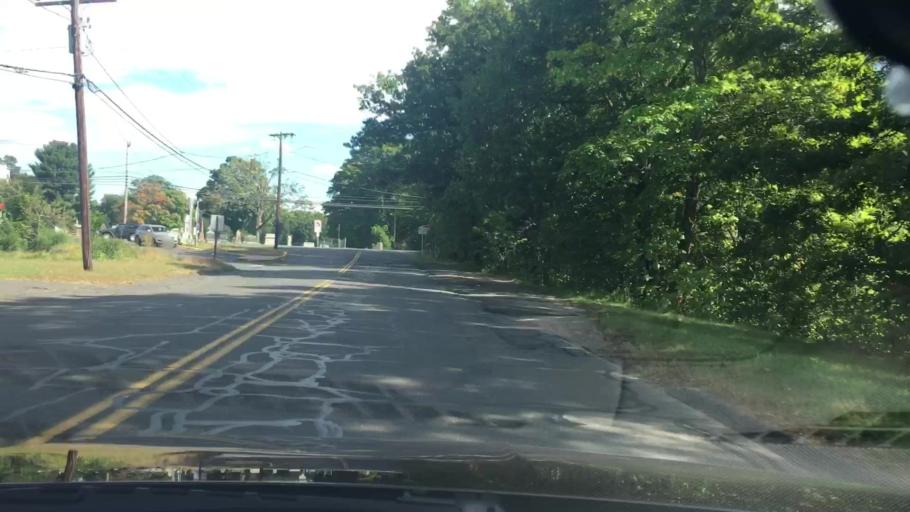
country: US
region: Connecticut
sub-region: Hartford County
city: Plainville
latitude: 41.6753
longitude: -72.8778
